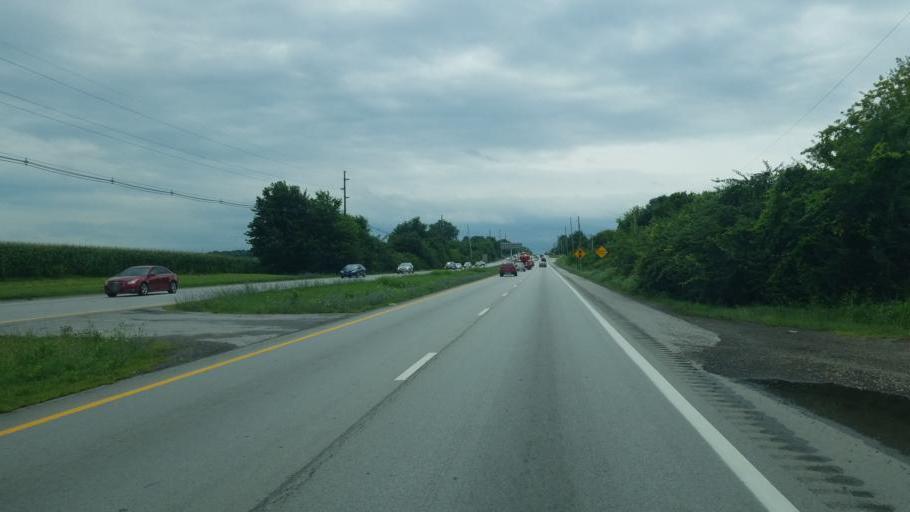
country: US
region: Ohio
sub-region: Franklin County
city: Obetz
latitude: 39.8669
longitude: -83.0051
